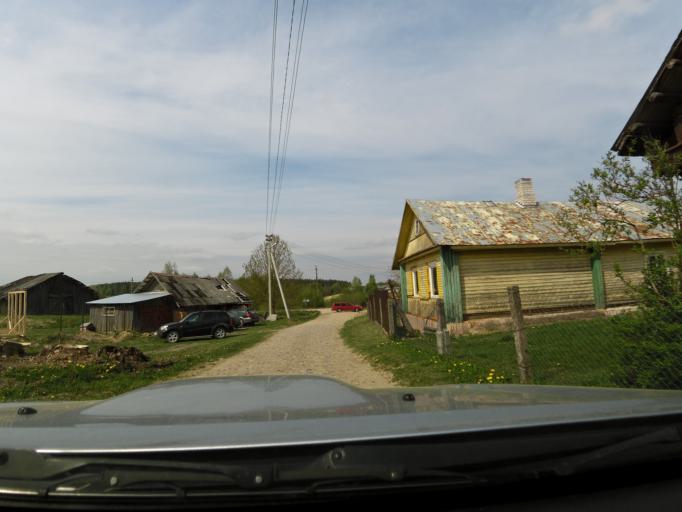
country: LT
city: Salcininkai
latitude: 54.4194
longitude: 25.3202
